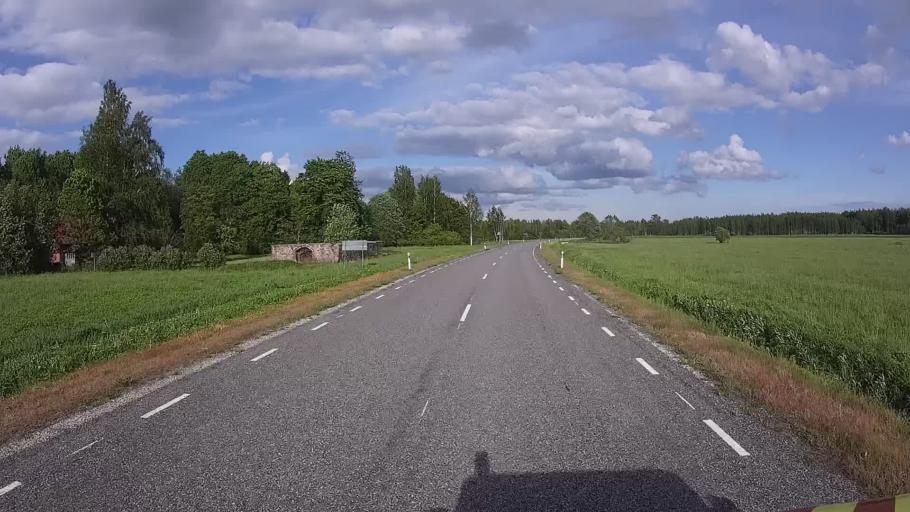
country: EE
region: Jogevamaa
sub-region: Mustvee linn
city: Mustvee
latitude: 59.0251
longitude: 27.0300
